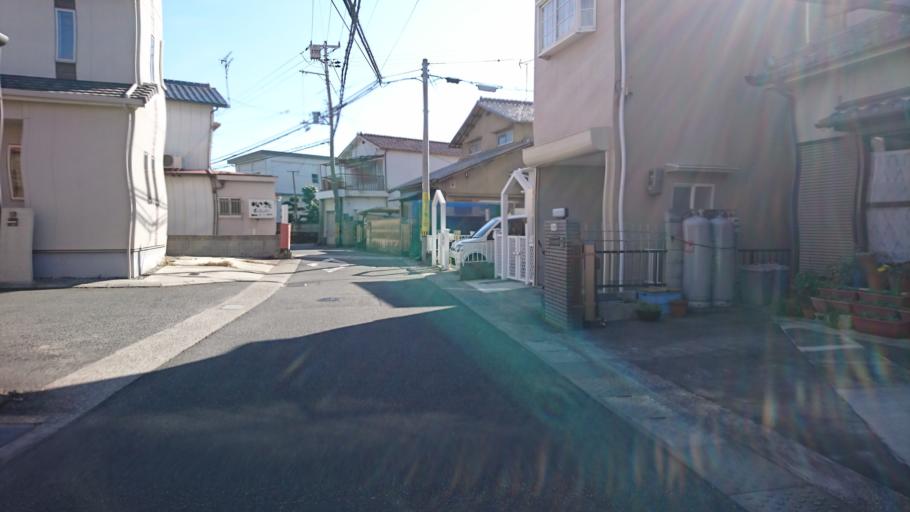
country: JP
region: Hyogo
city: Kakogawacho-honmachi
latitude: 34.7923
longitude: 134.7945
